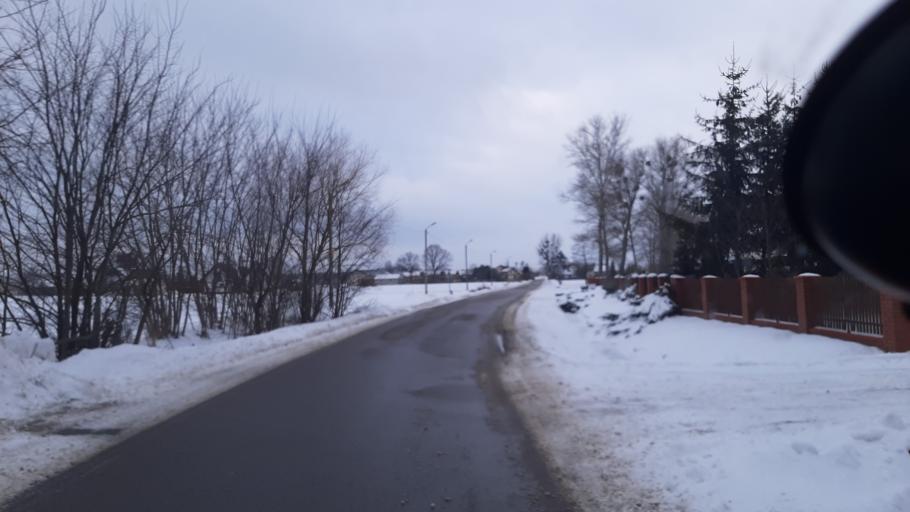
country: PL
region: Lublin Voivodeship
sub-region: Powiat lubartowski
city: Abramow
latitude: 51.4436
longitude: 22.2730
